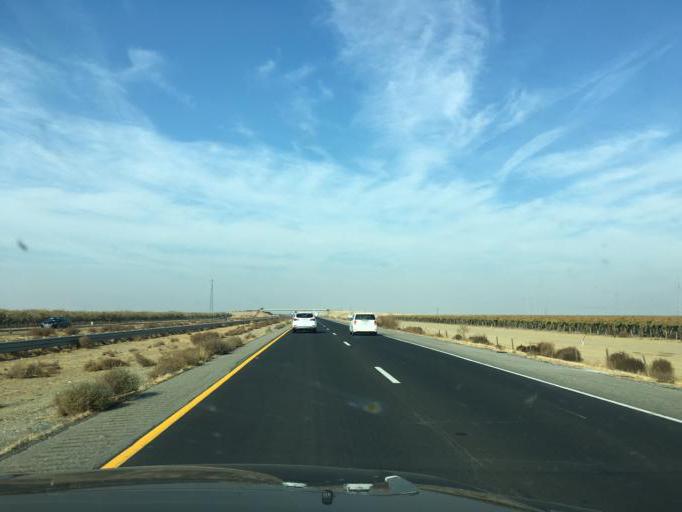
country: US
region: California
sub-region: Kings County
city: Kettleman City
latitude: 35.8707
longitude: -119.8479
